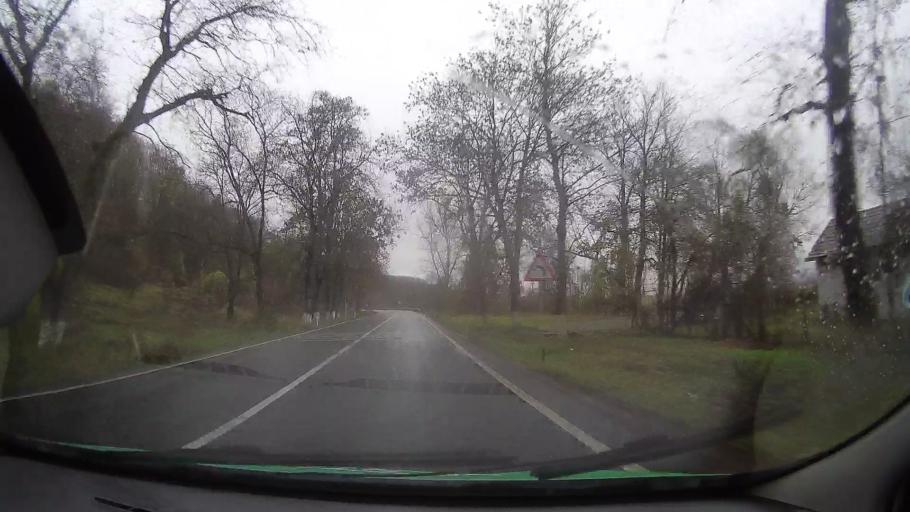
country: RO
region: Mures
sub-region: Comuna Brancovenesti
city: Brancovenesti
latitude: 46.8622
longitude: 24.7684
